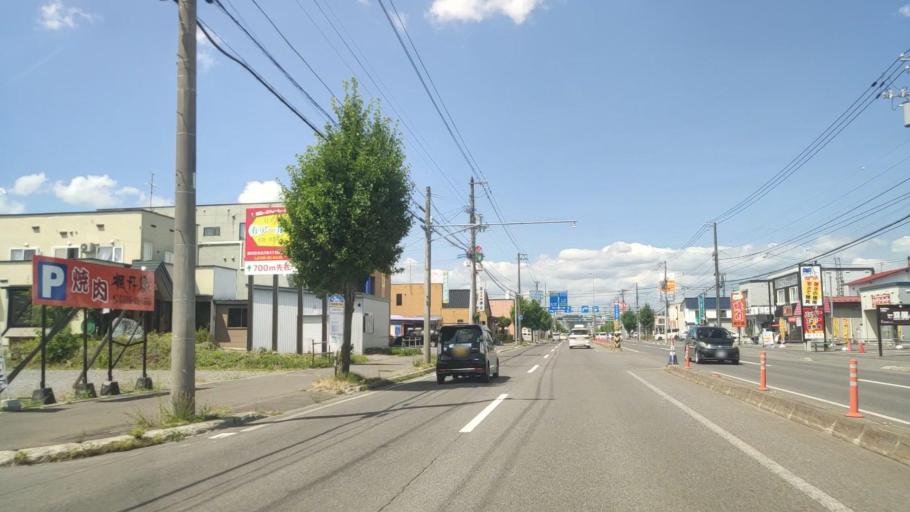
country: JP
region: Hokkaido
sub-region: Asahikawa-shi
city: Asahikawa
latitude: 43.8031
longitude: 142.3891
